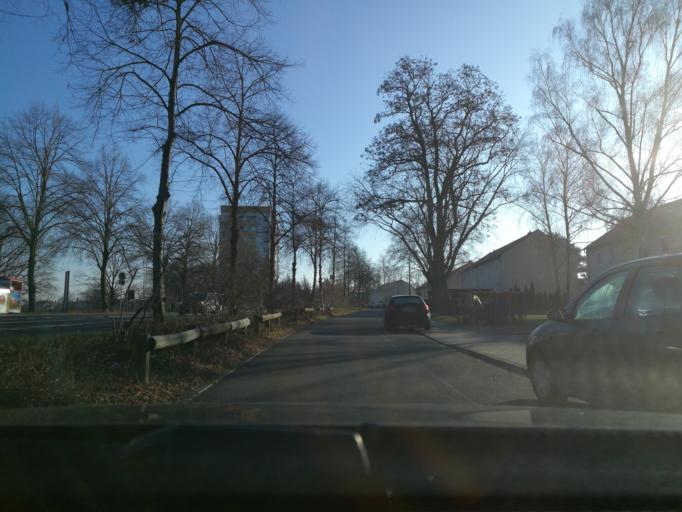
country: DE
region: Bavaria
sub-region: Regierungsbezirk Mittelfranken
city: Buckenhof
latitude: 49.5952
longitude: 11.0412
